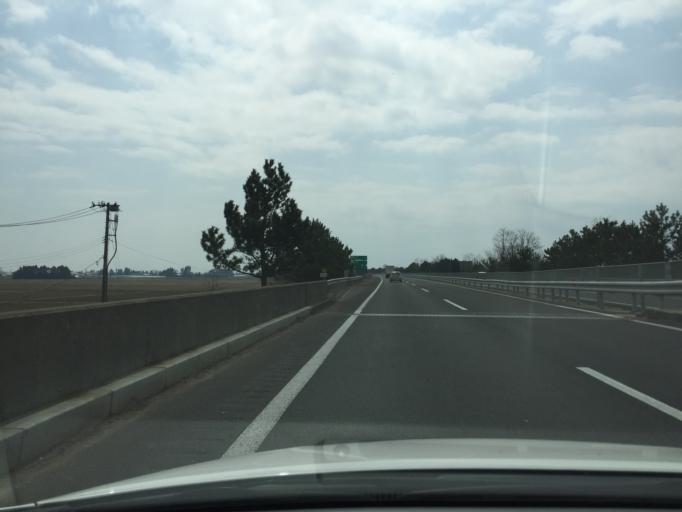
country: JP
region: Miyagi
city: Iwanuma
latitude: 38.1260
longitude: 140.8870
